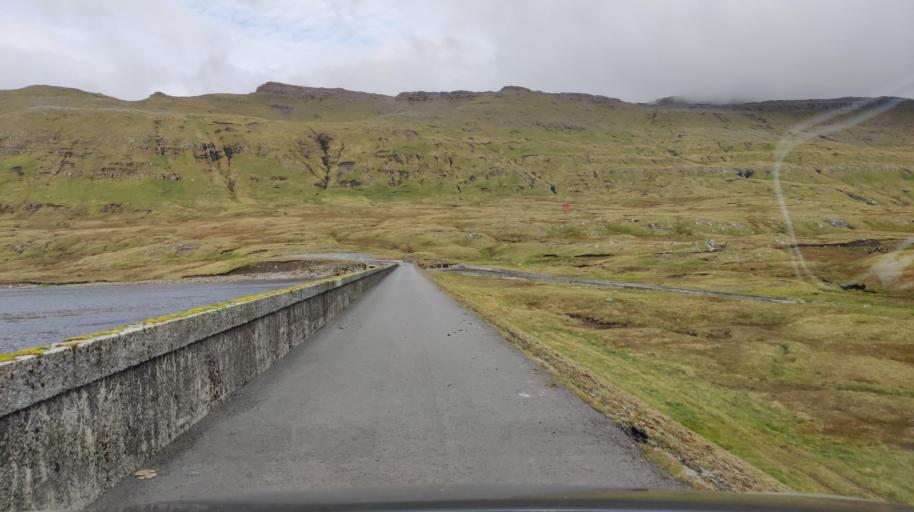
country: FO
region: Streymoy
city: Vestmanna
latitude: 62.1649
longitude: -7.0802
